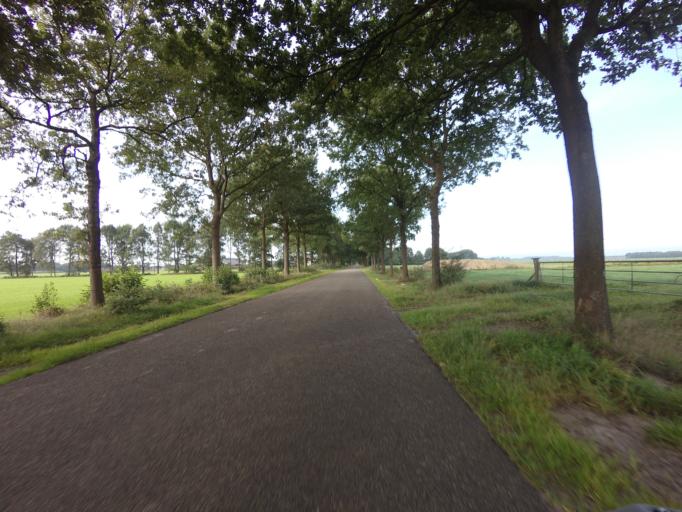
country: NL
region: Friesland
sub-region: Gemeente Weststellingwerf
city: Noordwolde
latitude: 52.9399
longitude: 6.2103
